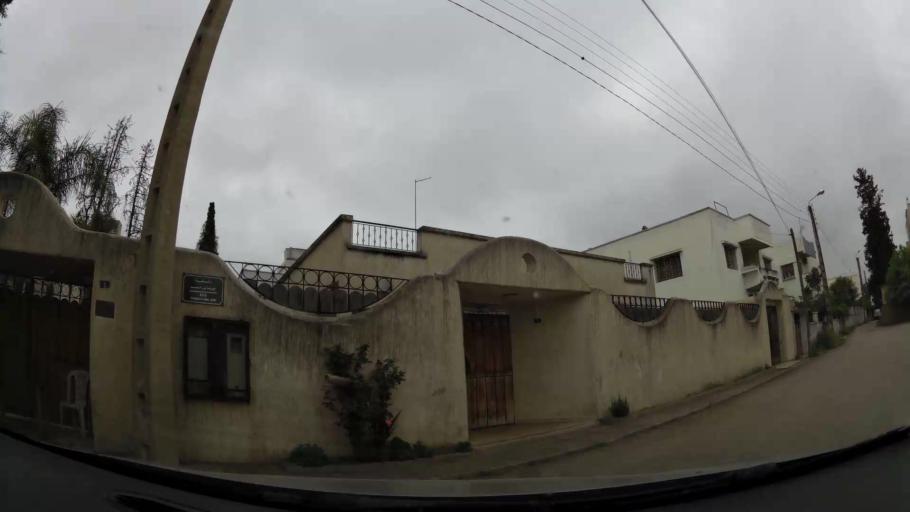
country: MA
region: Fes-Boulemane
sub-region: Fes
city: Fes
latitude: 34.0330
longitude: -5.0110
